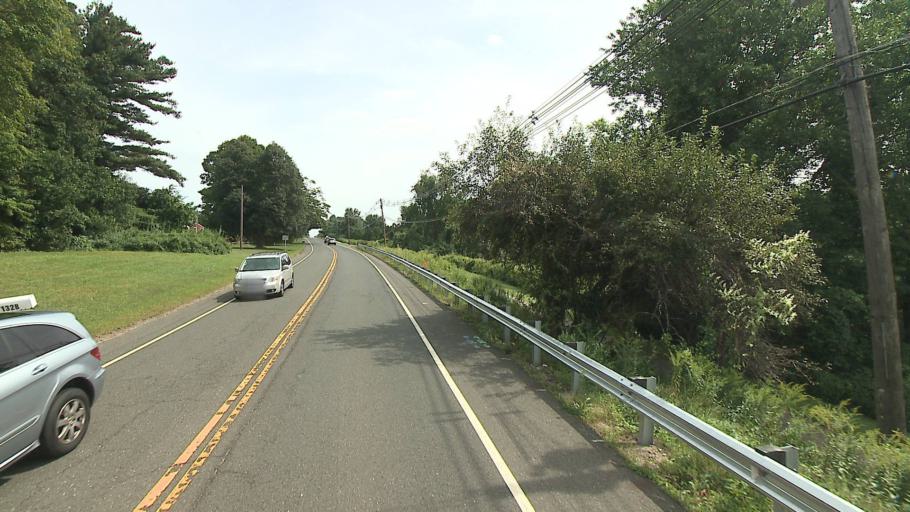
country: US
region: Connecticut
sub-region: Litchfield County
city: Watertown
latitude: 41.6170
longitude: -73.1026
